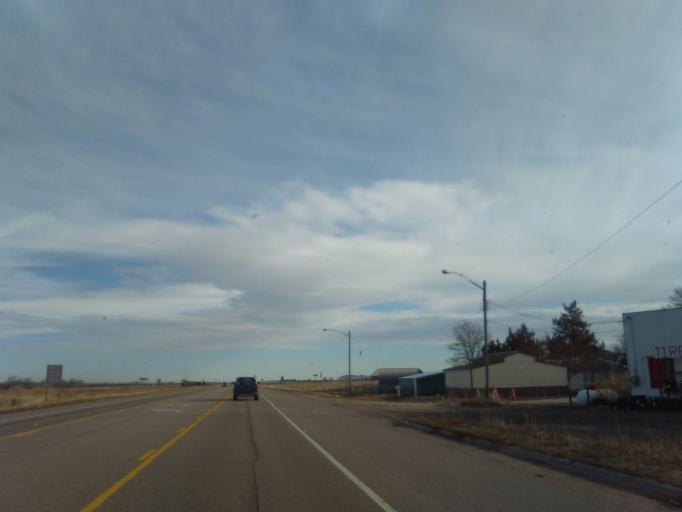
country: US
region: Nebraska
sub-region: Scotts Bluff County
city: Gering
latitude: 41.7834
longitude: -103.5164
